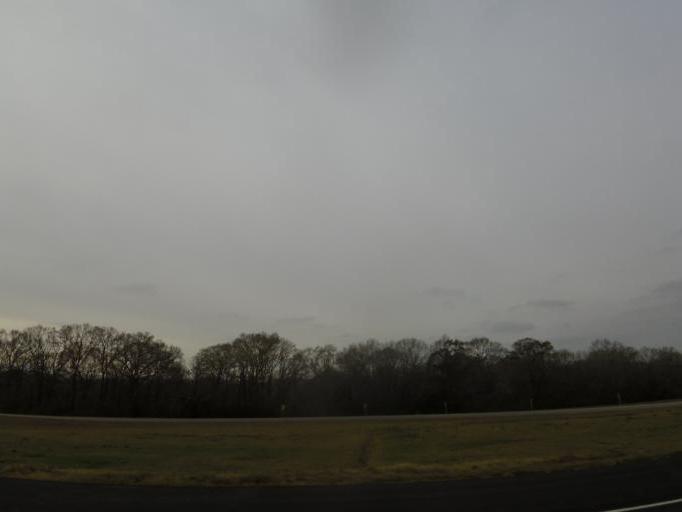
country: US
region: Alabama
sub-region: Elmore County
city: Millbrook
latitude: 32.4172
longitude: -86.3563
